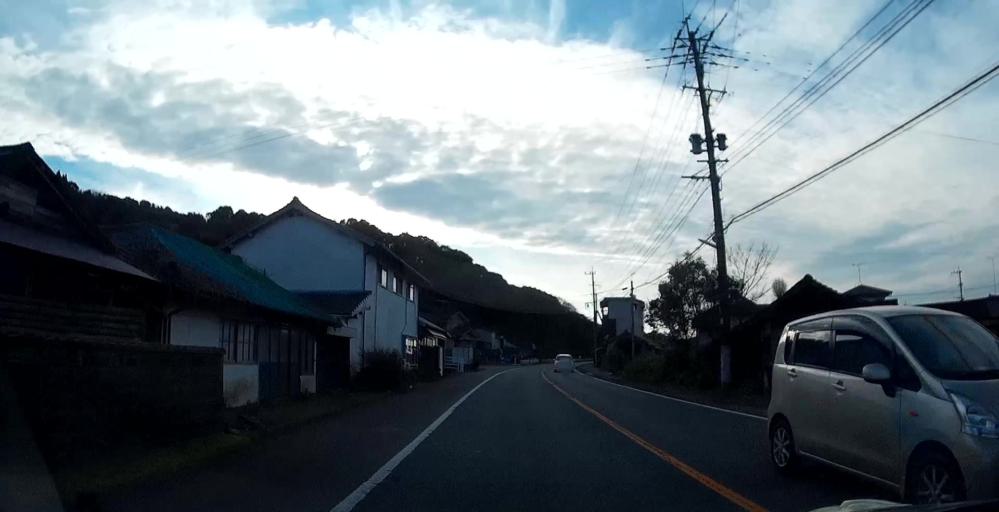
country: JP
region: Kumamoto
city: Uto
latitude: 32.6669
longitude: 130.5444
